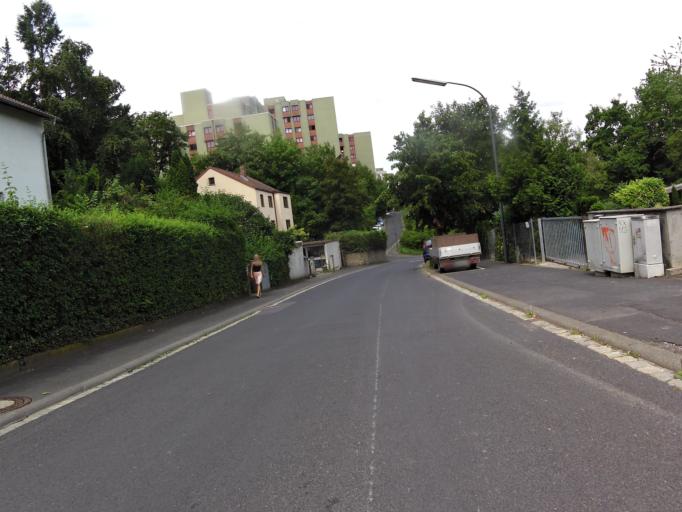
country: DE
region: Bavaria
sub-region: Regierungsbezirk Unterfranken
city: Wuerzburg
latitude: 49.7924
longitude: 9.9637
